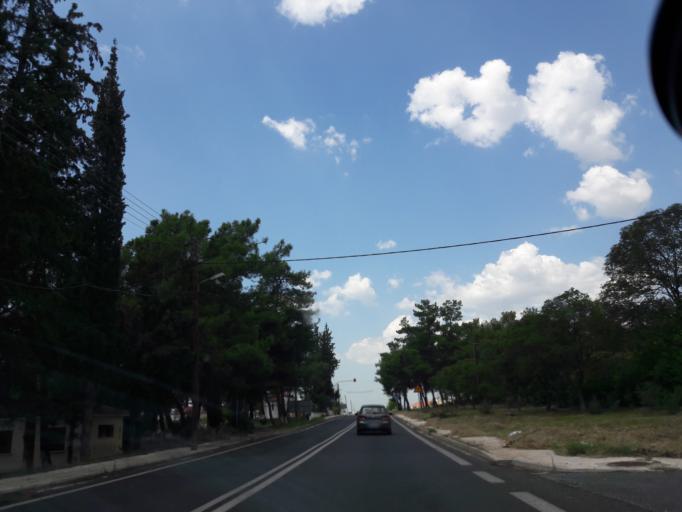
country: GR
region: Central Macedonia
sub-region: Nomos Thessalonikis
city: Agia Paraskevi
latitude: 40.5133
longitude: 23.0758
